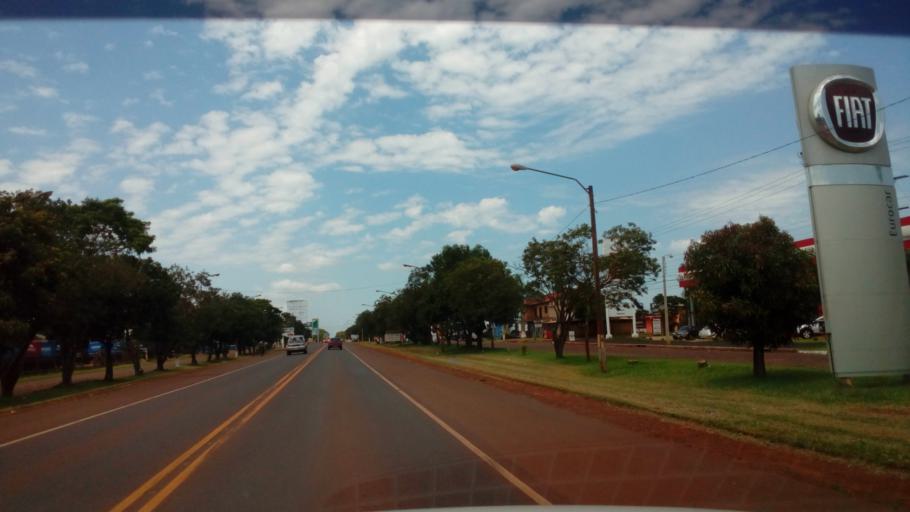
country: PY
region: Alto Parana
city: Santa Rita
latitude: -25.7766
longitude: -55.0747
